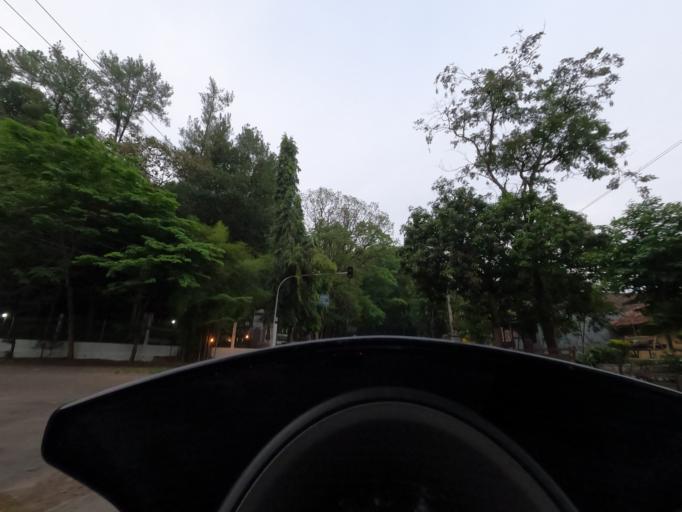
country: ID
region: West Java
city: Lembang
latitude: -6.5841
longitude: 107.7422
